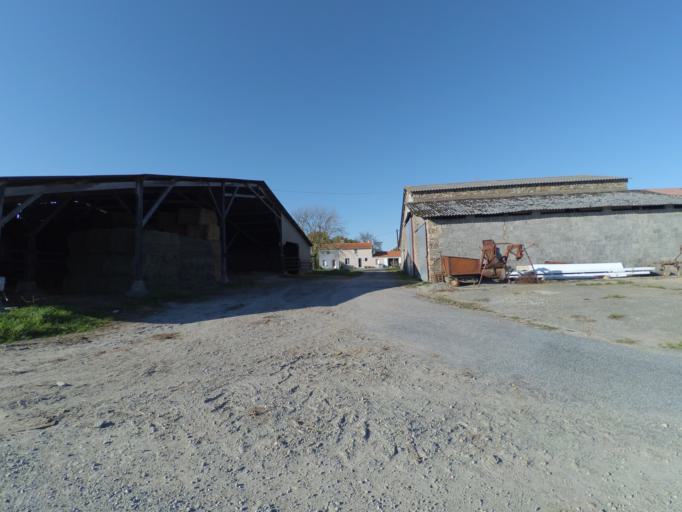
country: FR
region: Pays de la Loire
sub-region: Departement de la Vendee
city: Saint-Hilaire-de-Loulay
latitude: 47.0090
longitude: -1.3761
